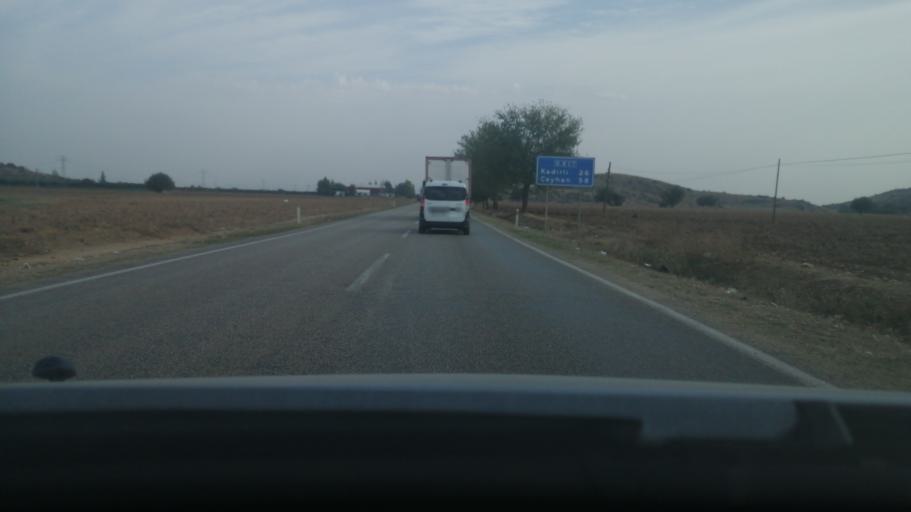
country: TR
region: Adana
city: Kozan
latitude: 37.3731
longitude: 35.8401
